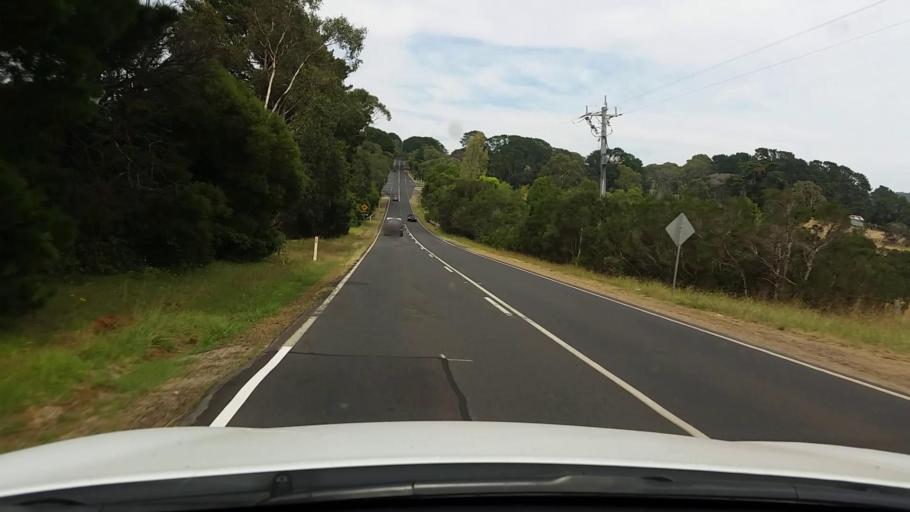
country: AU
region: Victoria
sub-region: Mornington Peninsula
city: Merricks
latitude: -38.4044
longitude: 145.0685
